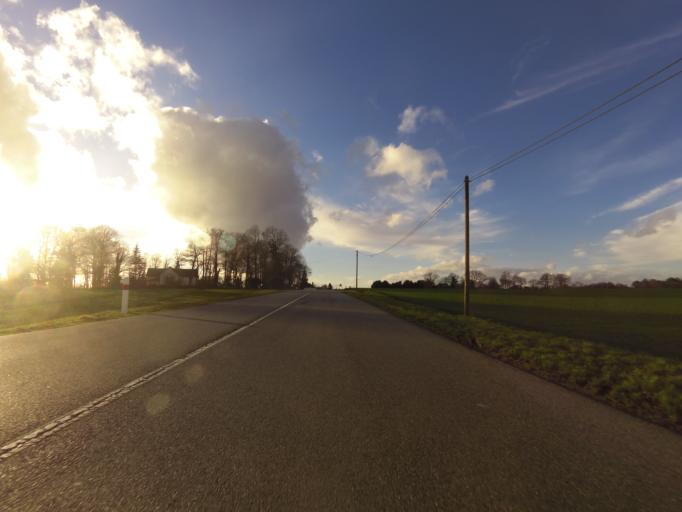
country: FR
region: Brittany
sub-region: Departement du Morbihan
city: Naizin
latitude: 48.0188
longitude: -2.8045
